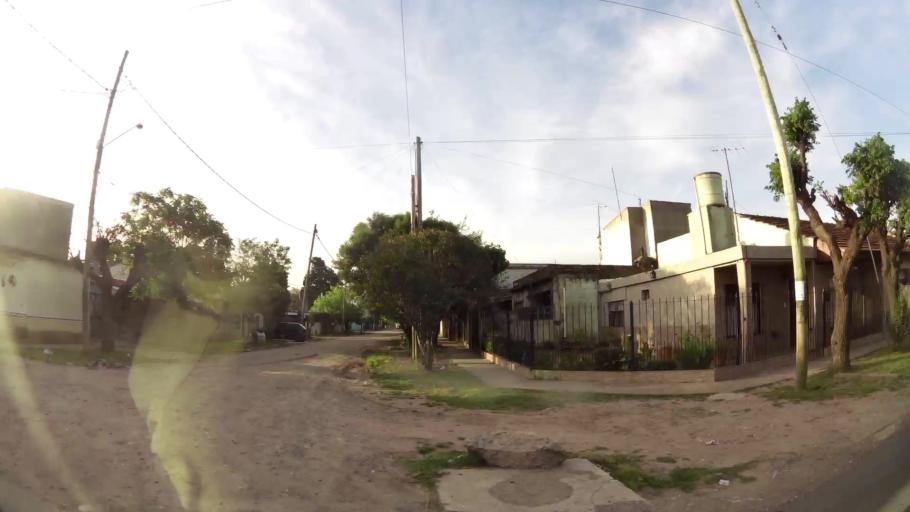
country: AR
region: Buenos Aires
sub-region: Partido de Almirante Brown
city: Adrogue
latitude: -34.7858
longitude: -58.3345
